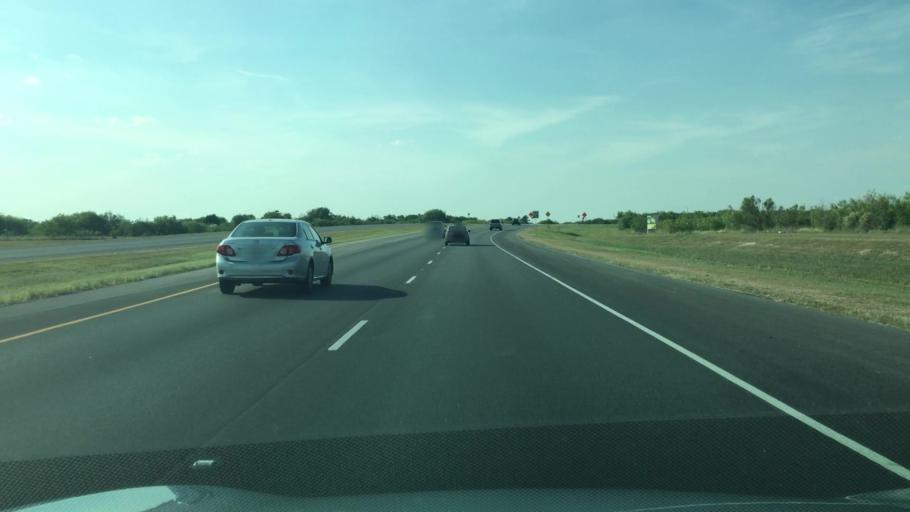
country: US
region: Texas
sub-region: Hays County
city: Kyle
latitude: 30.0422
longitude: -97.8740
